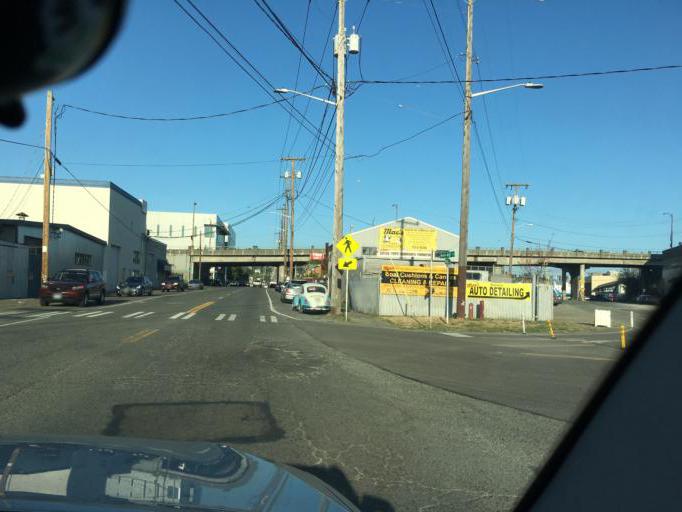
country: US
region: Washington
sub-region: King County
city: Seattle
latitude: 47.6622
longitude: -122.3779
